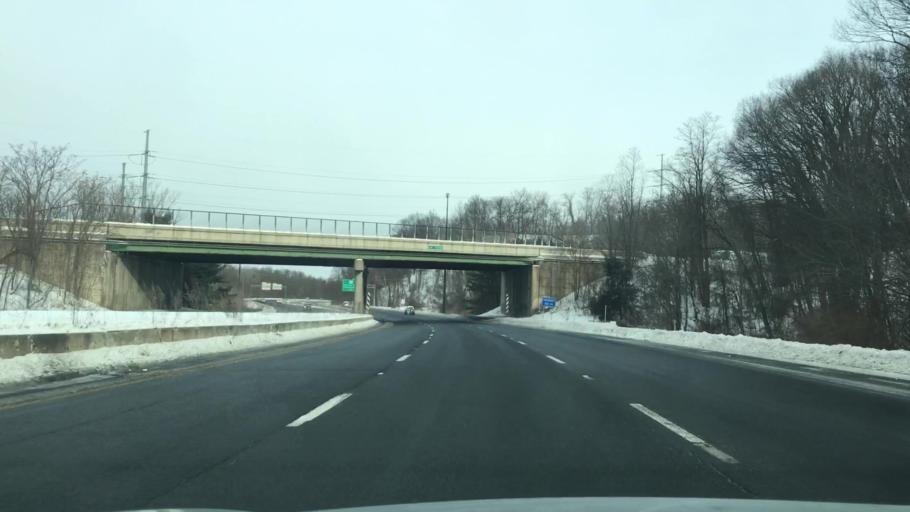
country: US
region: Massachusetts
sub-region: Hampden County
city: Chicopee
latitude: 42.1570
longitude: -72.6101
